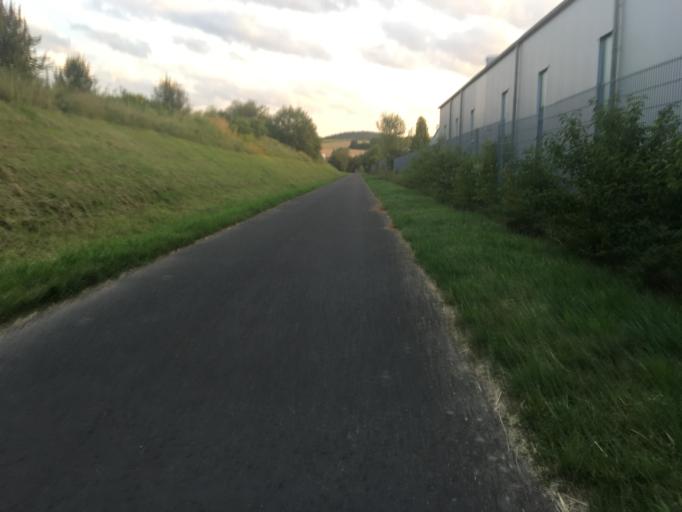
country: DE
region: Hesse
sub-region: Regierungsbezirk Darmstadt
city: Gelnhausen
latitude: 50.1873
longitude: 9.1864
